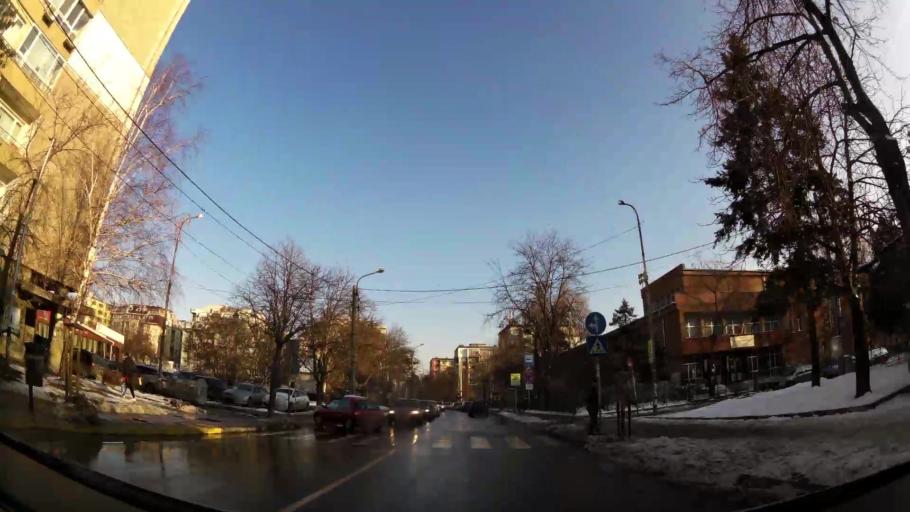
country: BG
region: Sofia-Capital
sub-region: Stolichna Obshtina
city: Sofia
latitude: 42.6834
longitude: 23.3618
